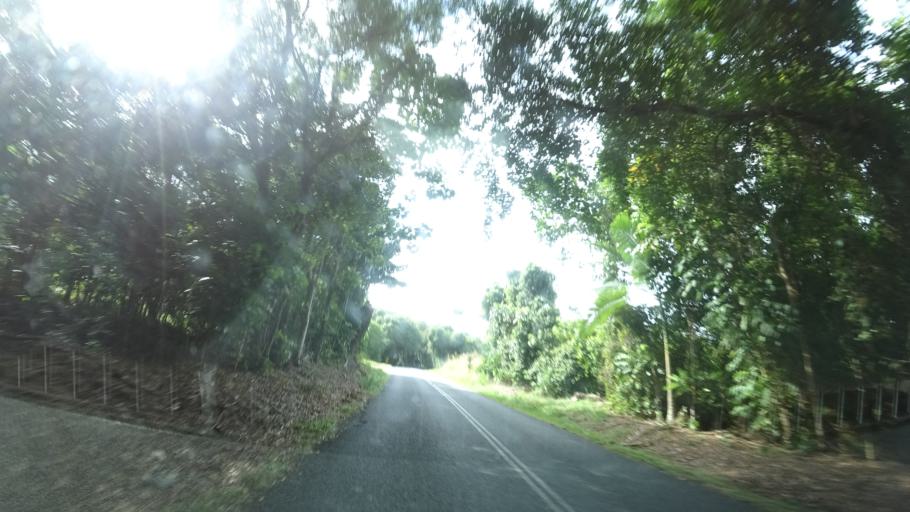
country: AU
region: Queensland
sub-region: Cairns
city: Port Douglas
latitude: -16.1010
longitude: 145.4587
